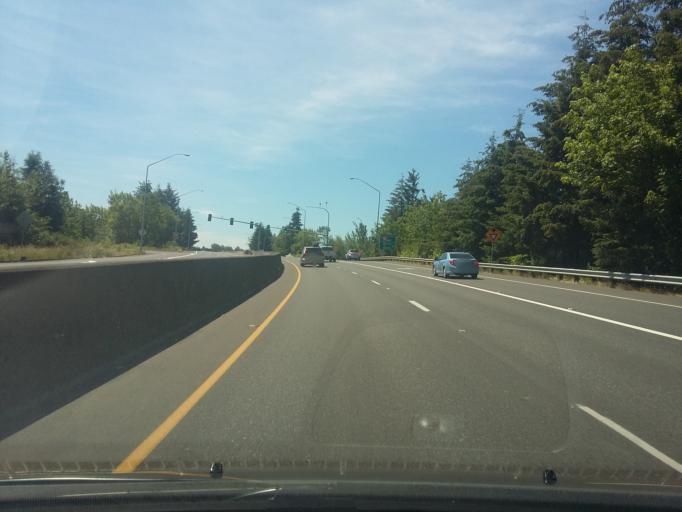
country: US
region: Washington
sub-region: Clark County
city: Barberton
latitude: 45.6837
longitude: -122.5900
